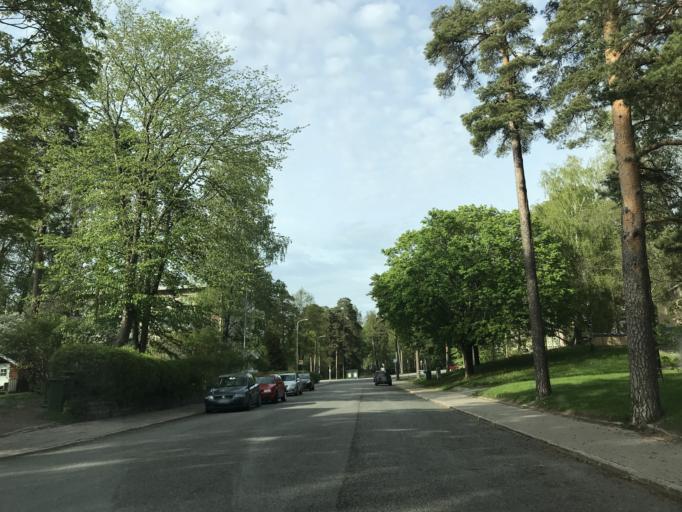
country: FI
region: Varsinais-Suomi
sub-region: Turku
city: Turku
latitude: 60.4365
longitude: 22.3020
